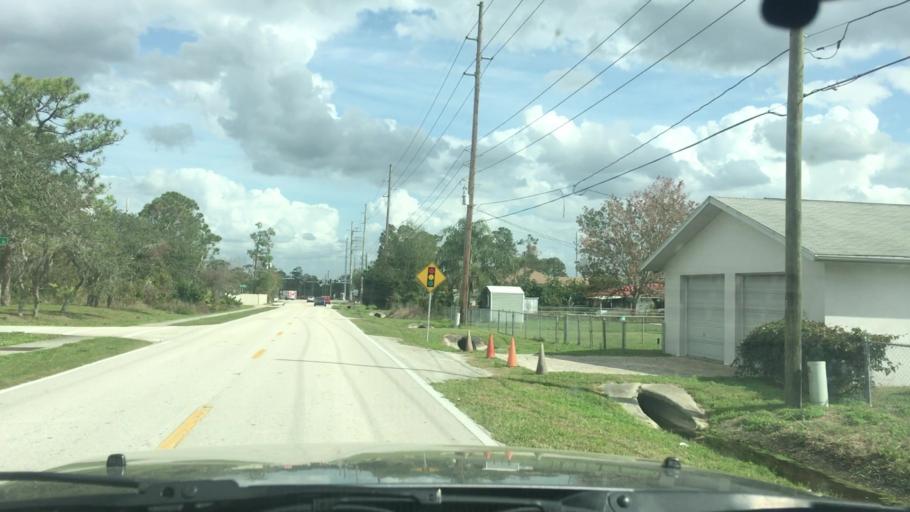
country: US
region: Florida
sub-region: Highlands County
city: Sebring
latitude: 27.5000
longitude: -81.4924
